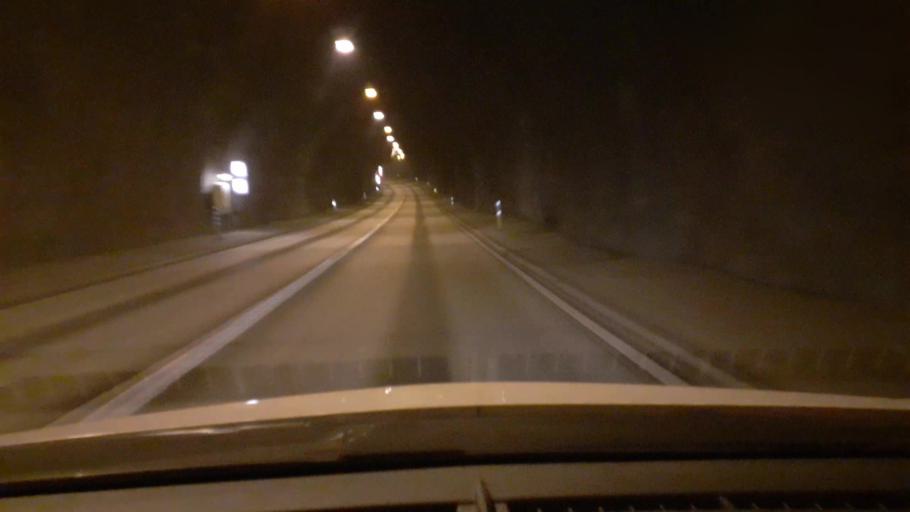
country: IS
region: Capital Region
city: Reykjavik
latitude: 64.3005
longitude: -21.8822
